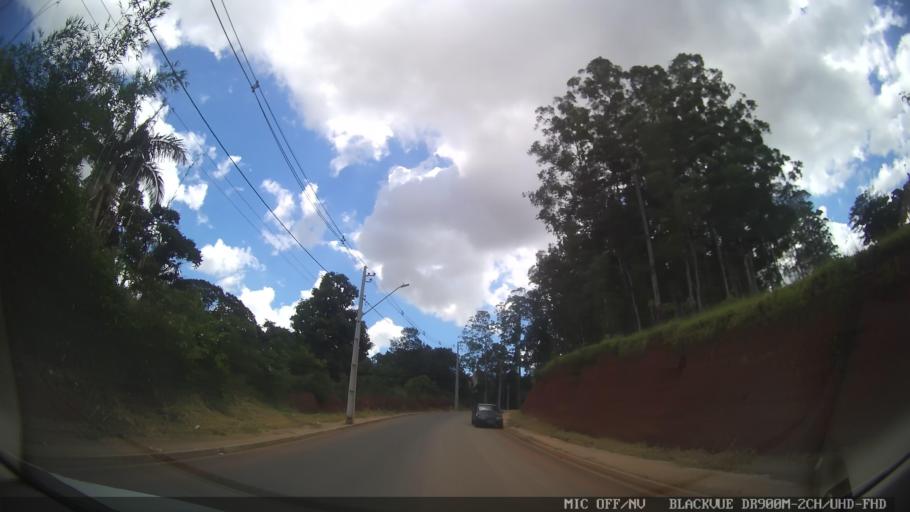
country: BR
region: Minas Gerais
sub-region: Extrema
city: Extrema
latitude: -22.8664
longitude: -46.3338
